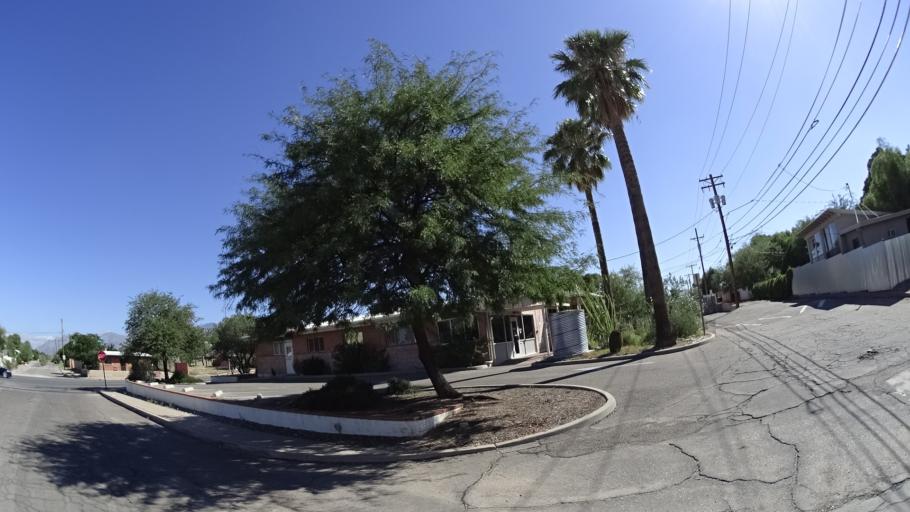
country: US
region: Arizona
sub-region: Pima County
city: Tucson
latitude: 32.2494
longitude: -110.9498
